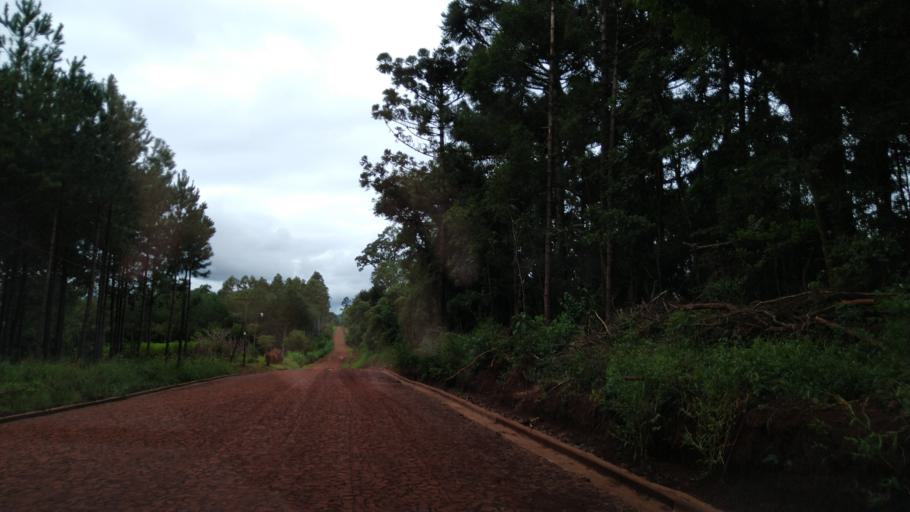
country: AR
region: Misiones
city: Capiovi
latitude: -26.9350
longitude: -55.0381
